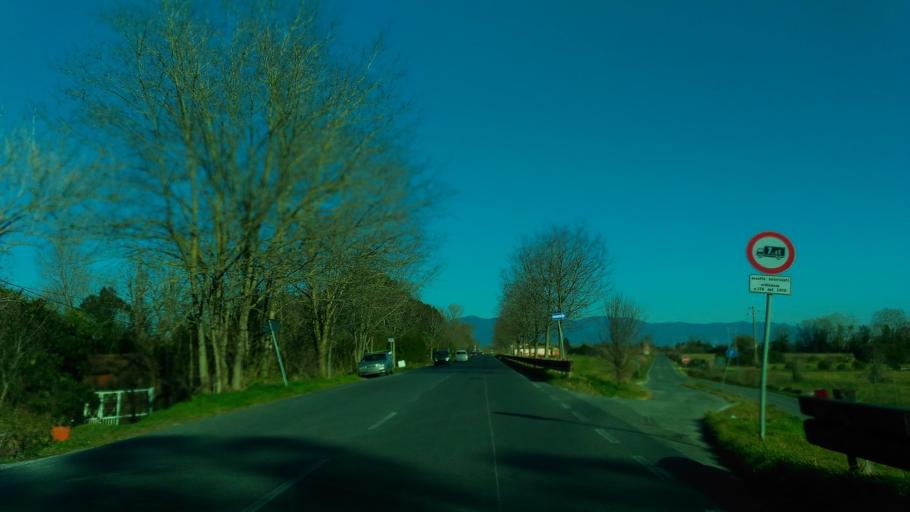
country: IT
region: Tuscany
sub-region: Province of Pisa
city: Marina di Pisa
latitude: 43.6783
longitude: 10.3276
